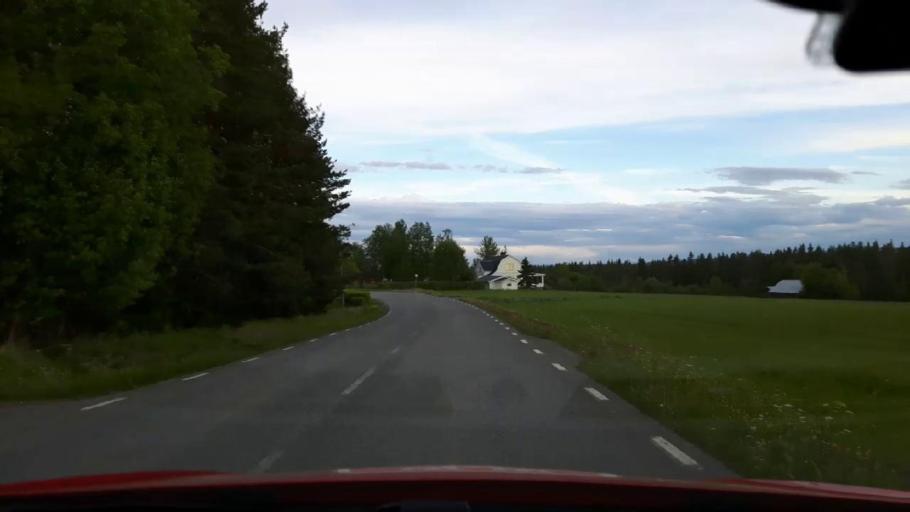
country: SE
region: Jaemtland
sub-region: Bergs Kommun
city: Hoverberg
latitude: 63.0330
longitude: 14.4700
